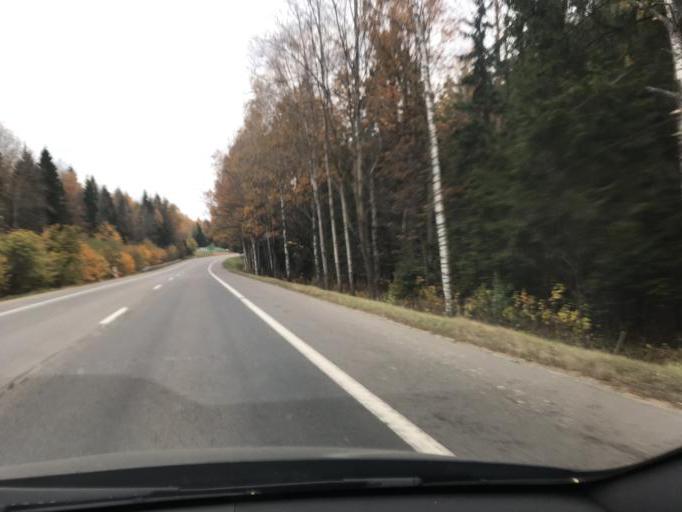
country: BY
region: Minsk
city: Korolev Stan
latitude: 54.0362
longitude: 27.8280
